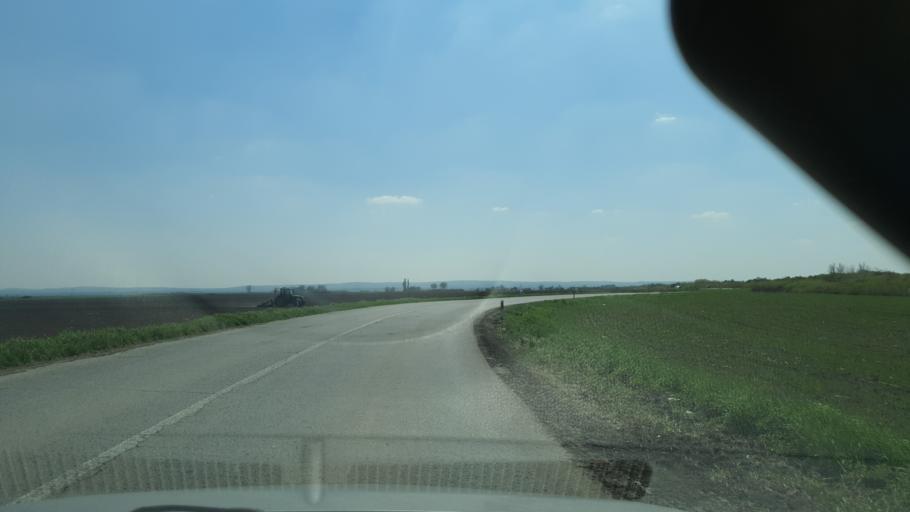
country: RS
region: Autonomna Pokrajina Vojvodina
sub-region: Juznobacki Okrug
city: Backa Palanka
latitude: 45.3130
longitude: 19.4417
